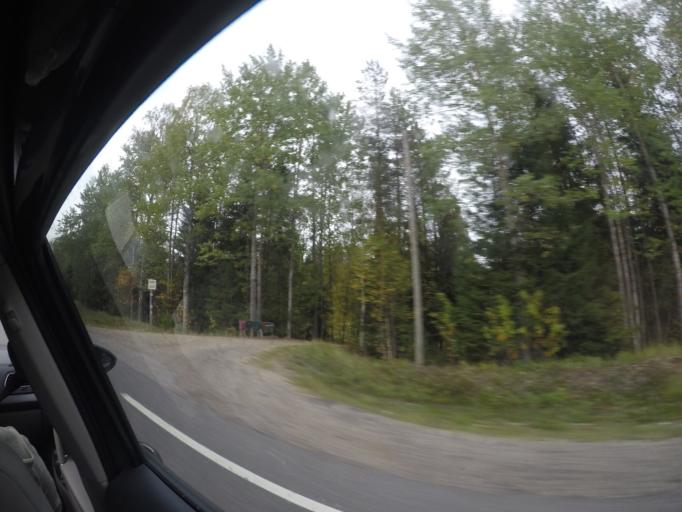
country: FI
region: Pirkanmaa
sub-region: Ylae-Pirkanmaa
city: Juupajoki
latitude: 61.7783
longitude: 24.3044
